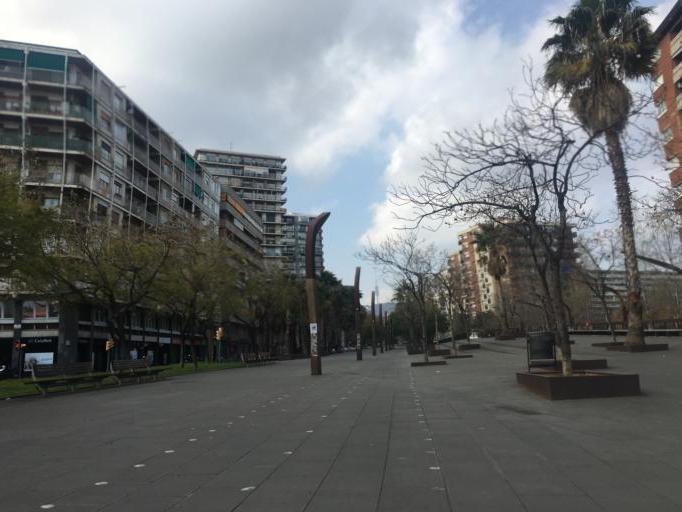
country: ES
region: Catalonia
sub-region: Provincia de Barcelona
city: les Corts
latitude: 41.3799
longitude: 2.1289
